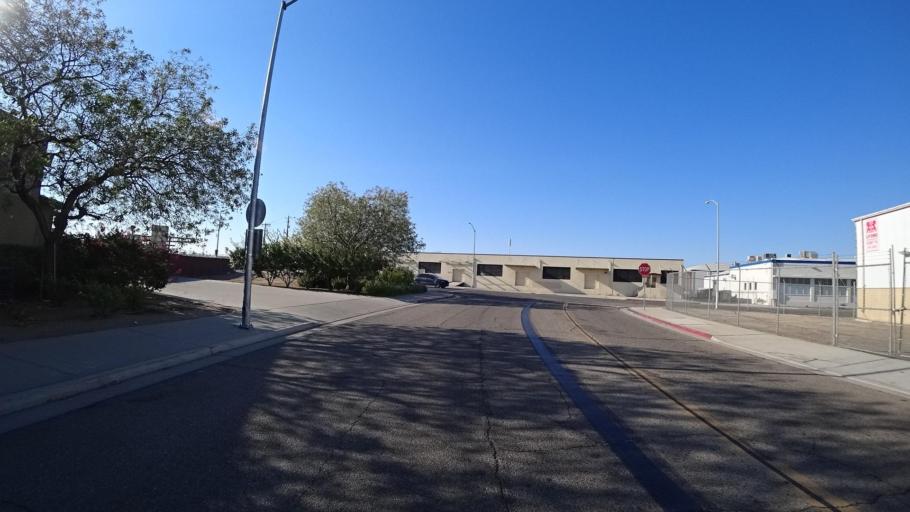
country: US
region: California
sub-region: Fresno County
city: Fresno
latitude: 36.7291
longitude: -119.7759
